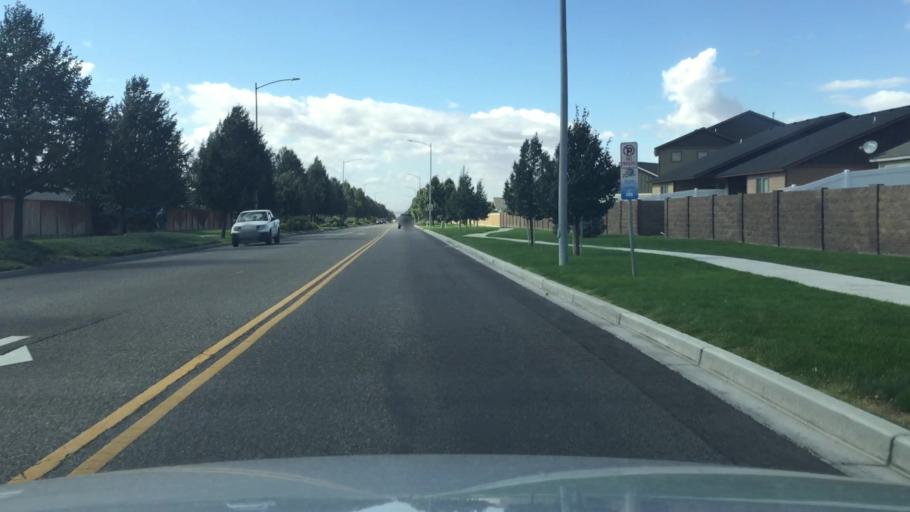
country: US
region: Washington
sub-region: Franklin County
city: West Pasco
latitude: 46.2780
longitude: -119.1904
